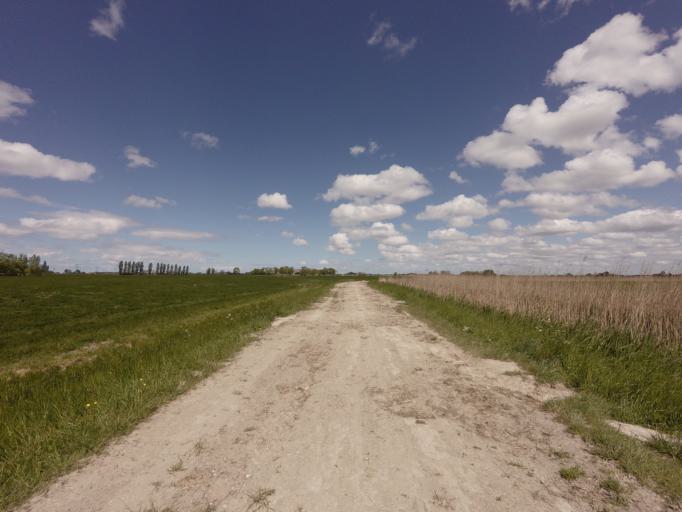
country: NL
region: Friesland
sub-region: Gemeente Franekeradeel
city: Franeker
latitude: 53.1454
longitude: 5.5038
